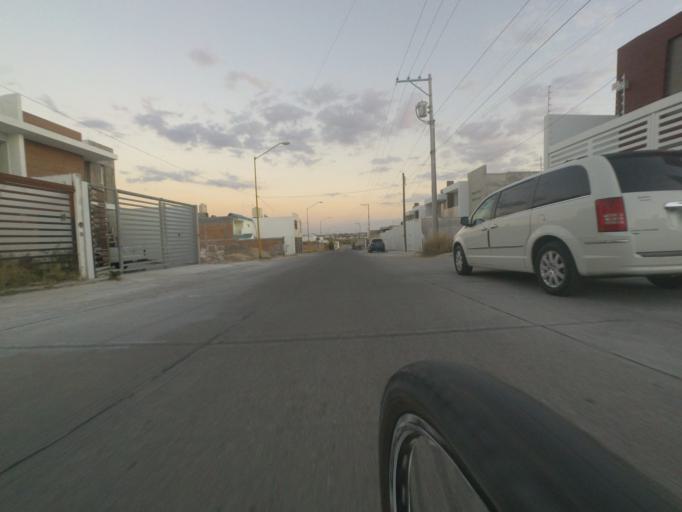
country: MX
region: Aguascalientes
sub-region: Aguascalientes
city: La Loma de los Negritos
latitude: 21.8518
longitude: -102.3363
